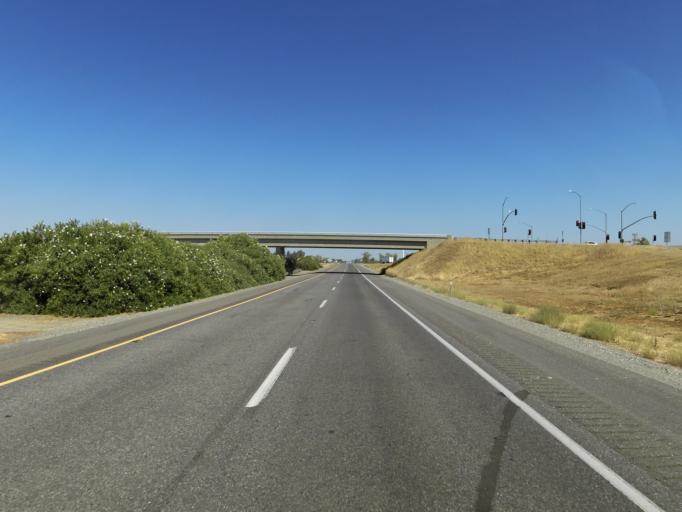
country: US
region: California
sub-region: Tehama County
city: Corning
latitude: 39.9055
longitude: -122.2000
